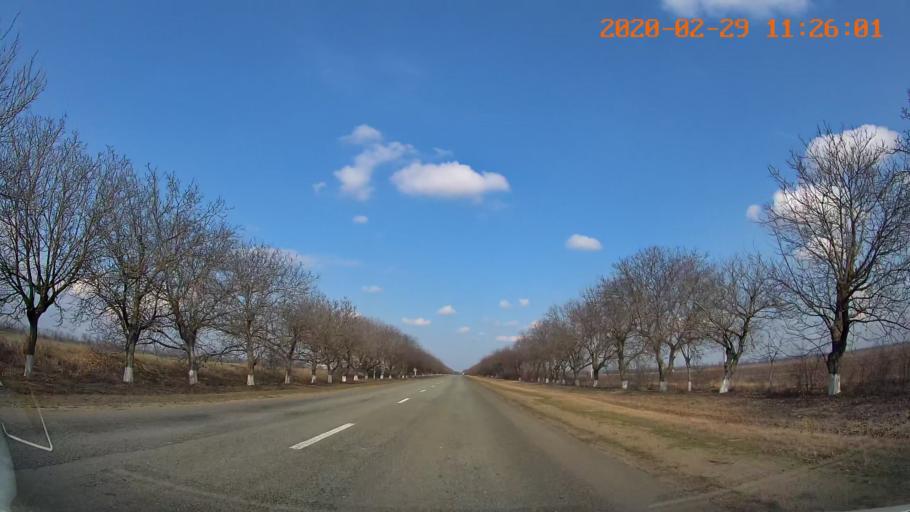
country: MD
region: Telenesti
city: Cocieri
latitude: 47.4472
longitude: 29.1478
